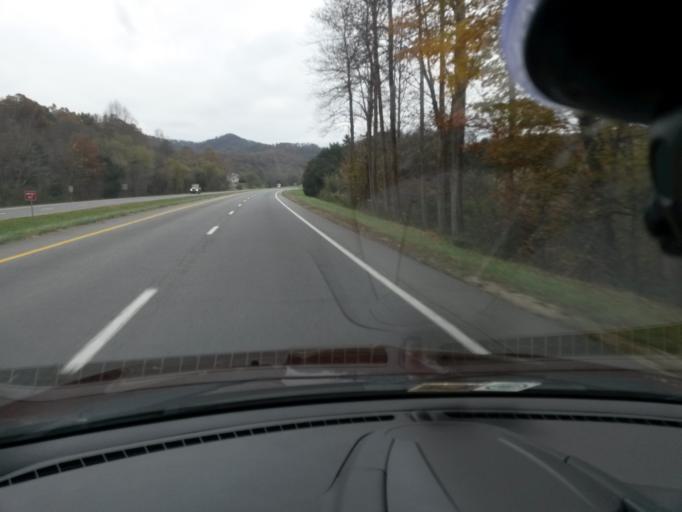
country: US
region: Virginia
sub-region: Albemarle County
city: Crozet
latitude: 37.9034
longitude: -78.6932
